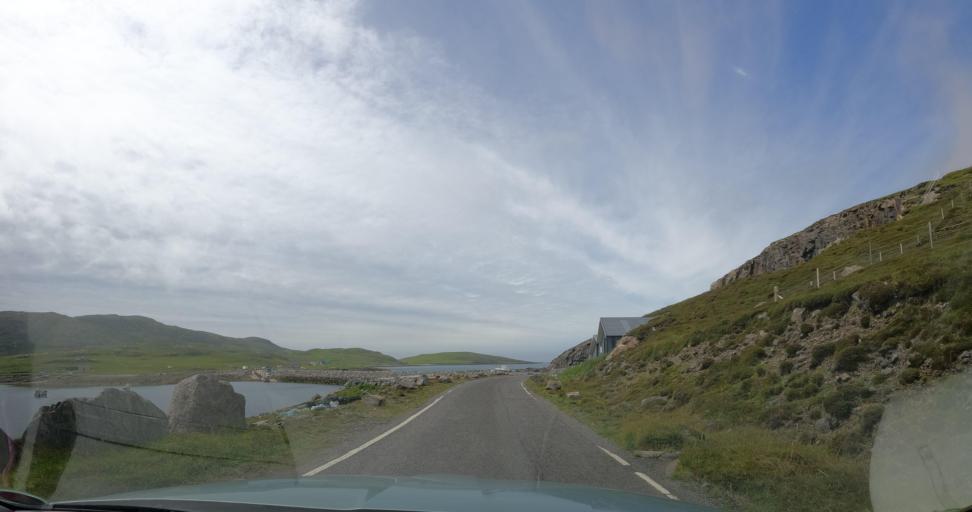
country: GB
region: Scotland
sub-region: Eilean Siar
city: Barra
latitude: 56.9476
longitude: -7.5288
